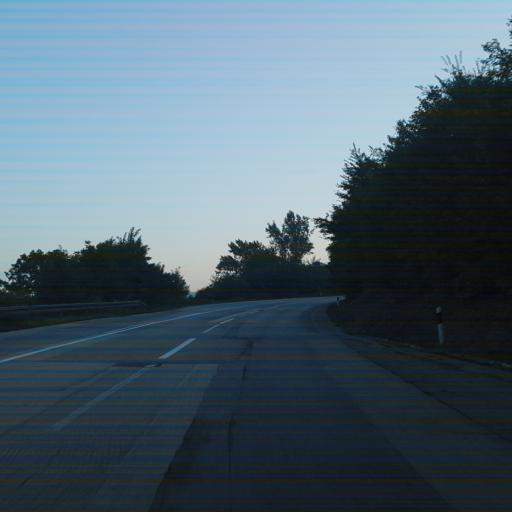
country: RS
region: Central Serbia
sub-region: Zajecarski Okrug
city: Zajecar
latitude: 43.9851
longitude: 22.2956
